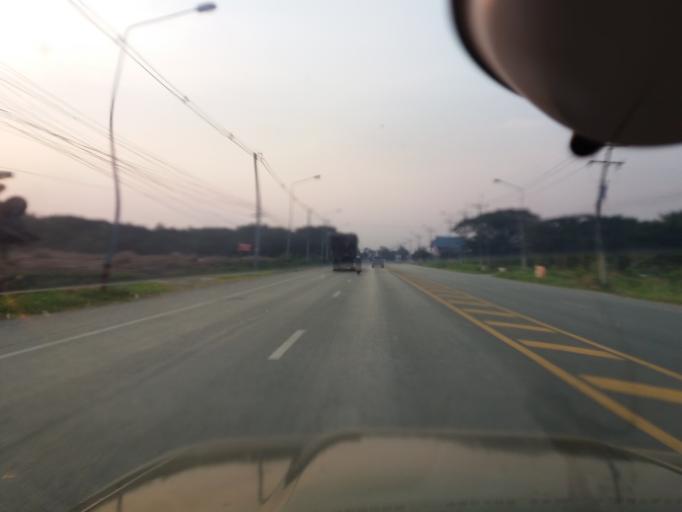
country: TH
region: Sing Buri
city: Sing Buri
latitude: 14.8850
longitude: 100.3766
